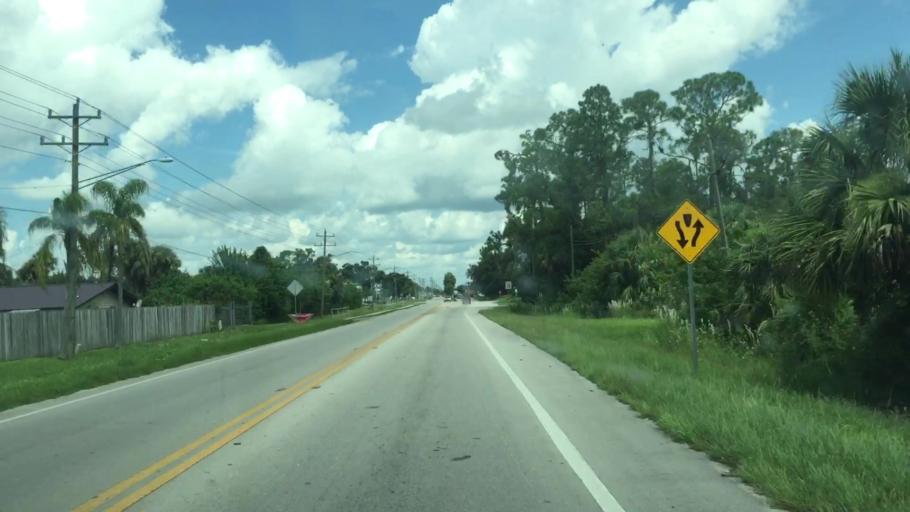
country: US
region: Florida
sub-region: Collier County
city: Immokalee
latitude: 26.4079
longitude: -81.4172
